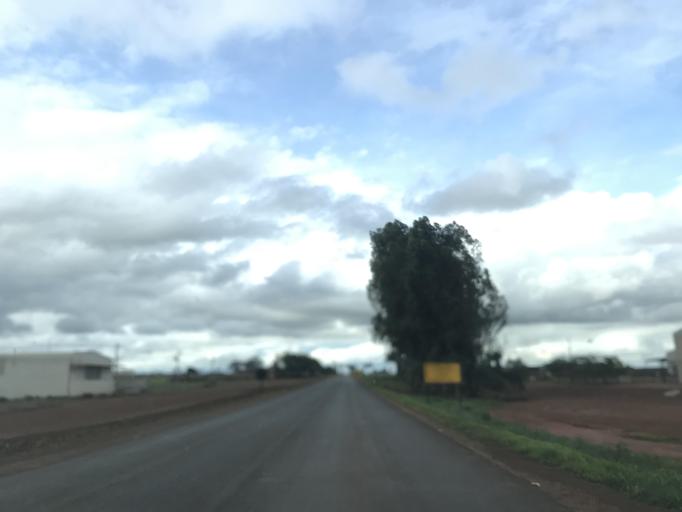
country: BR
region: Goias
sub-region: Vianopolis
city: Vianopolis
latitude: -16.7684
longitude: -48.5225
